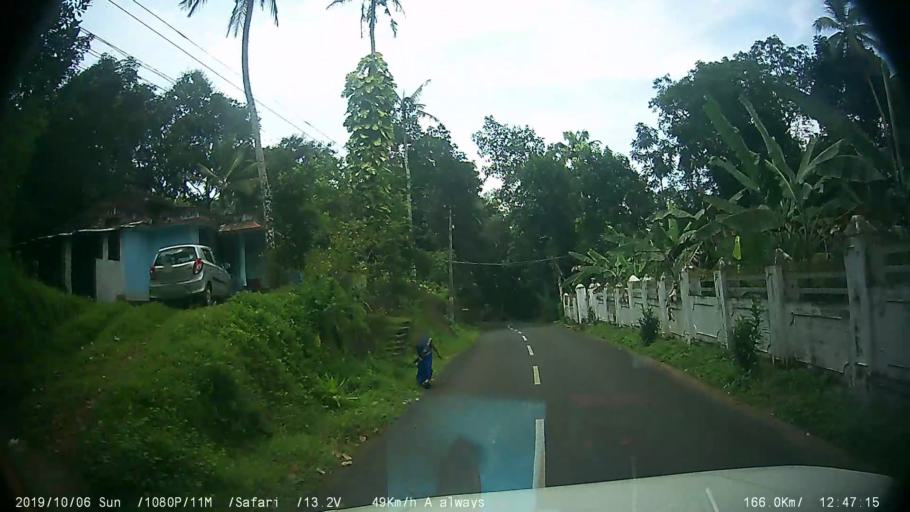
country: IN
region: Kerala
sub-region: Kottayam
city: Palackattumala
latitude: 9.7735
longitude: 76.6025
